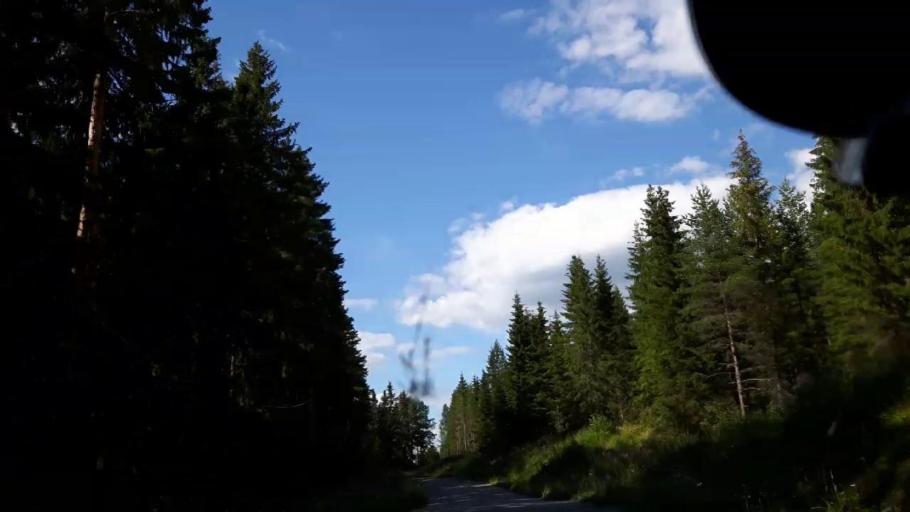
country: SE
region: Jaemtland
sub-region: Braecke Kommun
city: Braecke
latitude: 62.8648
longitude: 15.2724
